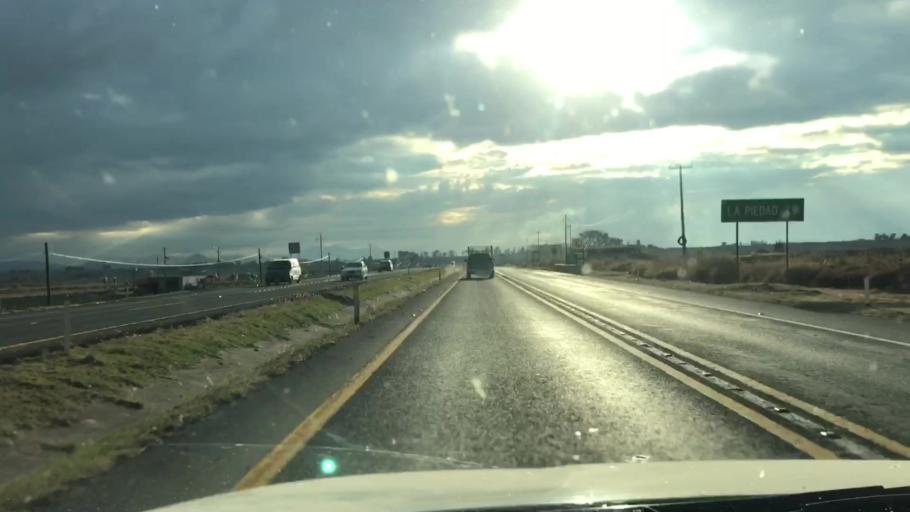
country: MX
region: Guanajuato
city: Penjamo
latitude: 20.3956
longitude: -101.7565
